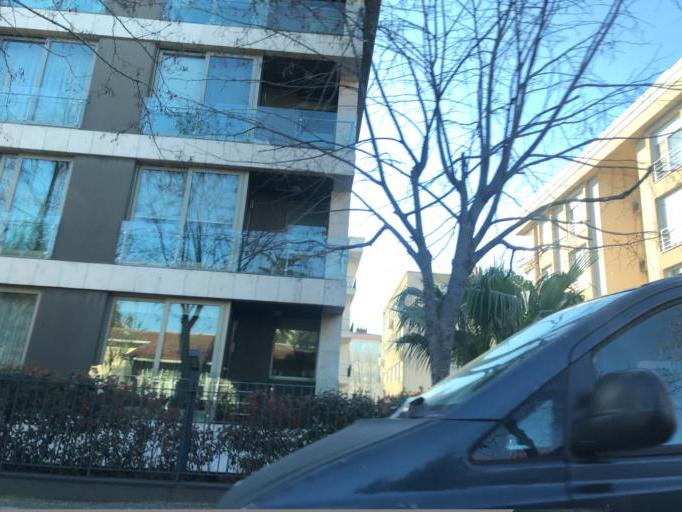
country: TR
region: Istanbul
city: Bahcelievler
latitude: 40.9628
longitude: 28.8337
